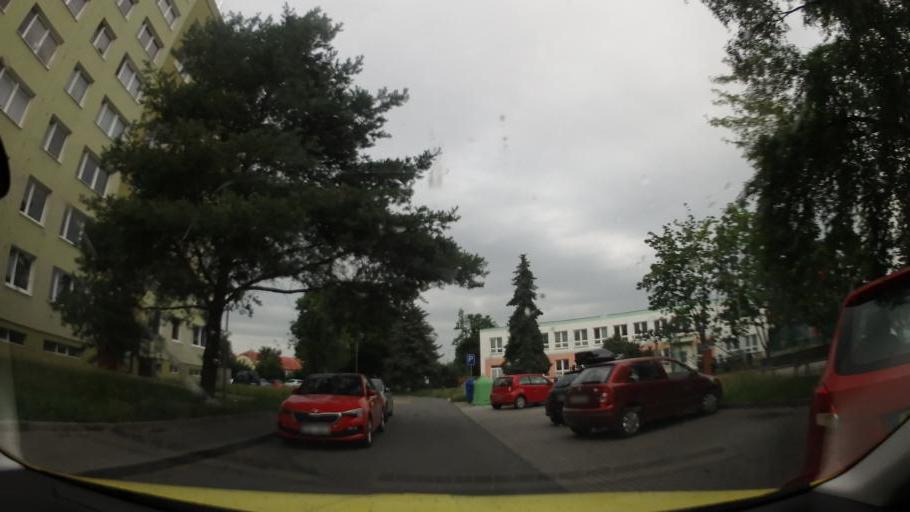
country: CZ
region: Olomoucky
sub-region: Okres Prerov
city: Hranice
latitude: 49.5542
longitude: 17.7328
